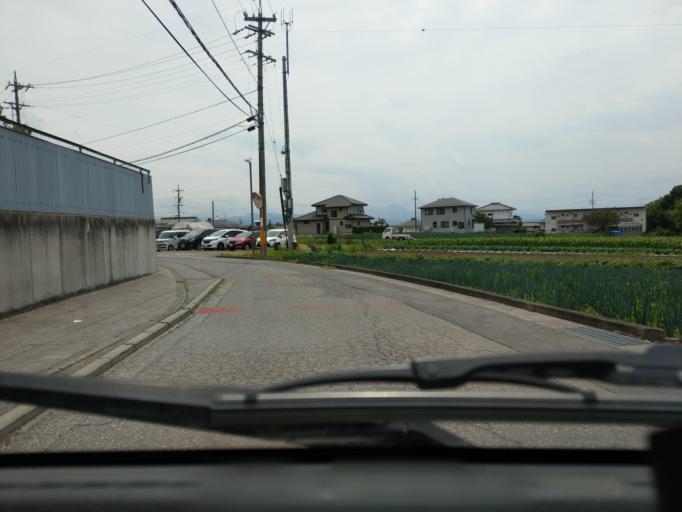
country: JP
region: Nagano
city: Komoro
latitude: 36.3190
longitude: 138.4541
